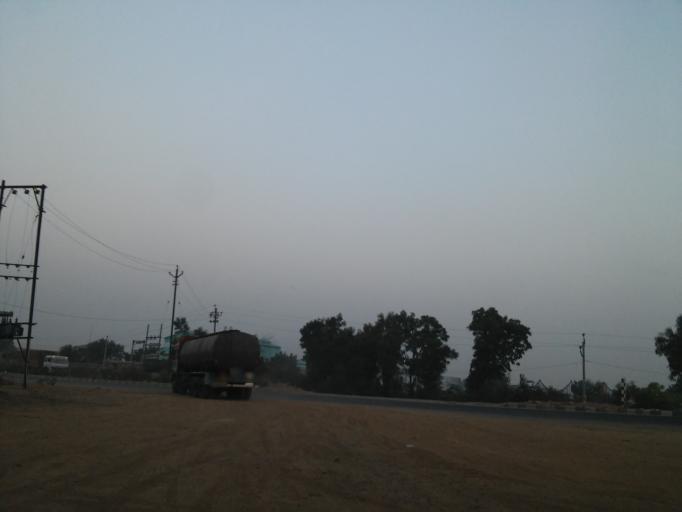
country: IN
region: Gujarat
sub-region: Surendranagar
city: Dhrangadhra
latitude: 22.9997
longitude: 71.4144
